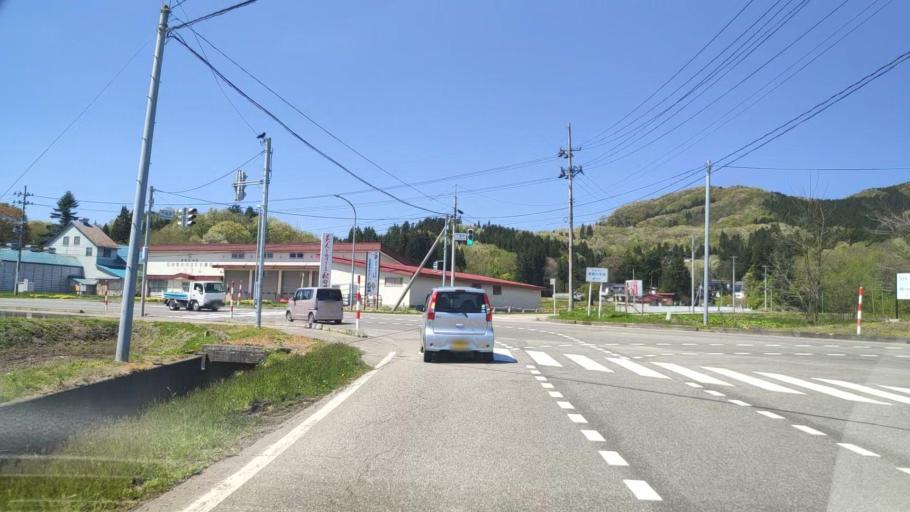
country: JP
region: Akita
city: Omagari
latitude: 39.4465
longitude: 140.4486
